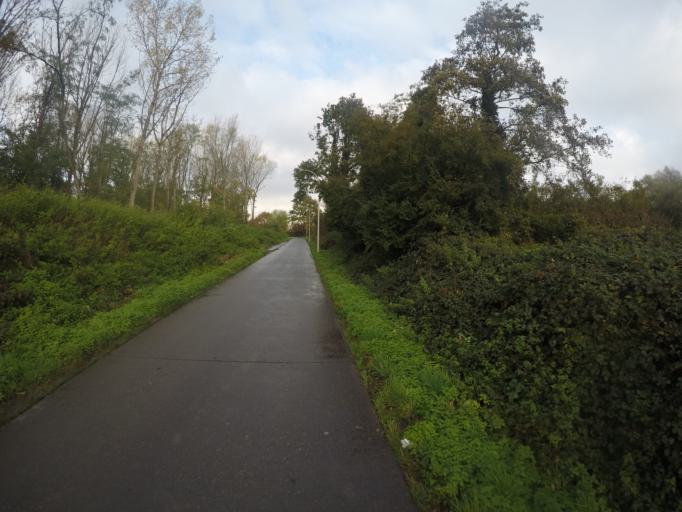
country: BE
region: Flanders
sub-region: Provincie Antwerpen
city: Zwijndrecht
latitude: 51.2055
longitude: 4.3058
